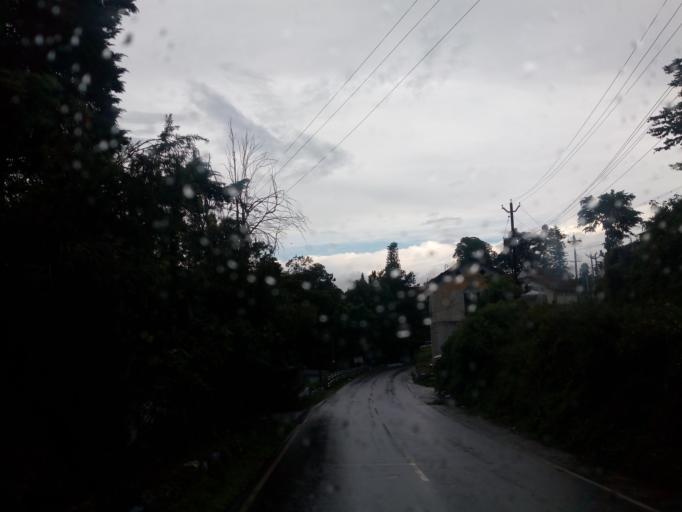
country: IN
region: Tamil Nadu
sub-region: Nilgiri
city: Wellington
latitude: 11.3450
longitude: 76.8020
